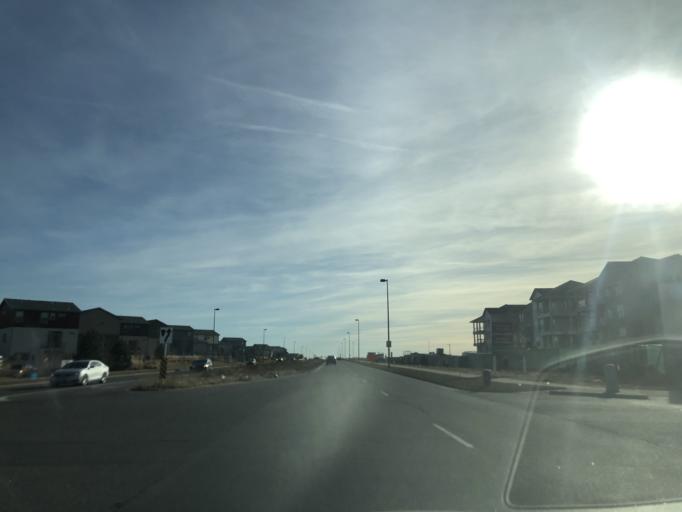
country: US
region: Colorado
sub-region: Adams County
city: Aurora
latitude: 39.7927
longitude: -104.7719
